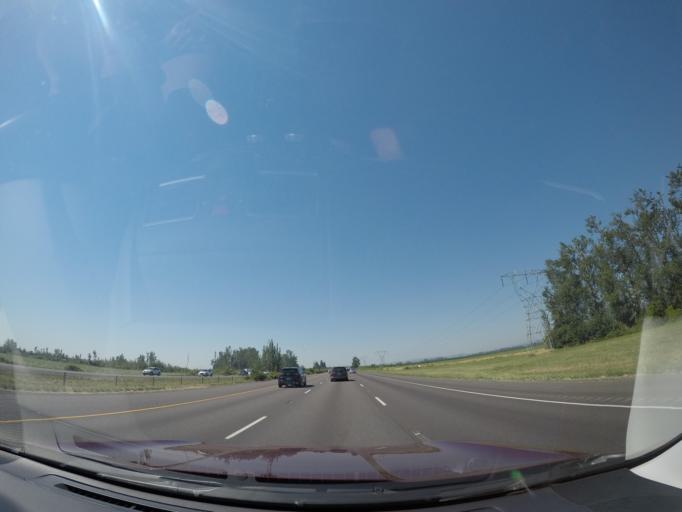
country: US
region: Oregon
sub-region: Marion County
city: Gervais
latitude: 45.0944
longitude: -122.9386
